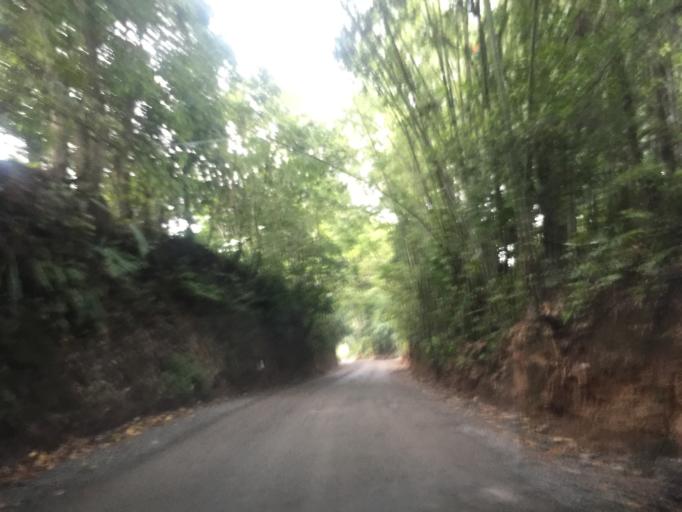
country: CO
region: Quindio
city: La Tebaida
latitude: 4.4628
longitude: -75.8047
